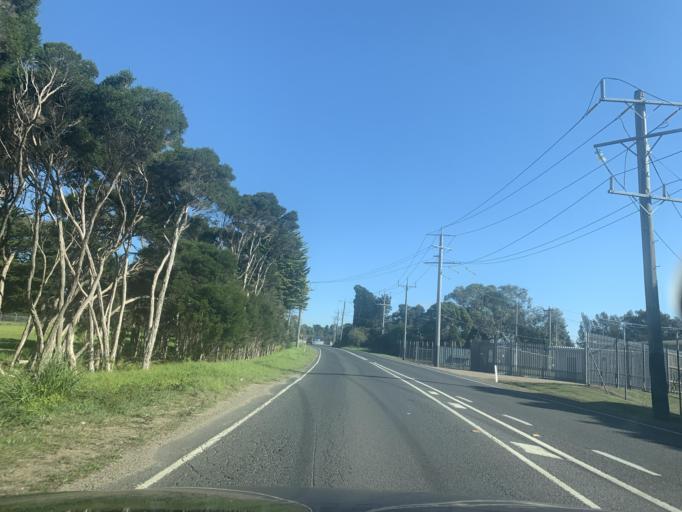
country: AU
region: Victoria
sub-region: Mornington Peninsula
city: Hastings
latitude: -38.2893
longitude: 145.1934
